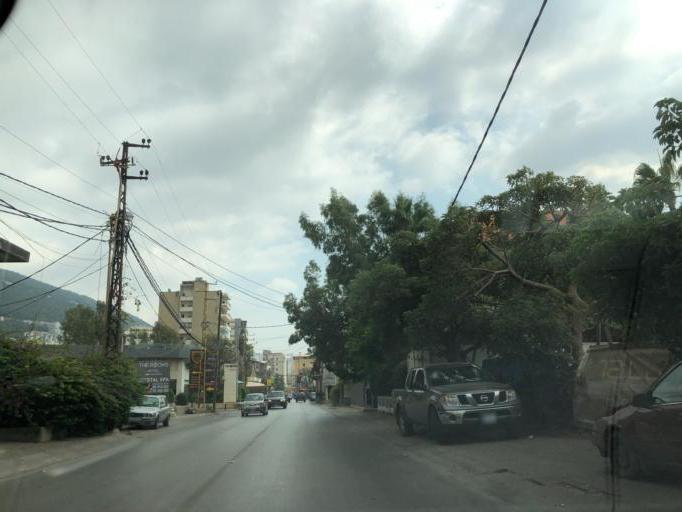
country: LB
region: Mont-Liban
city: Djounie
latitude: 33.9917
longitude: 35.6393
